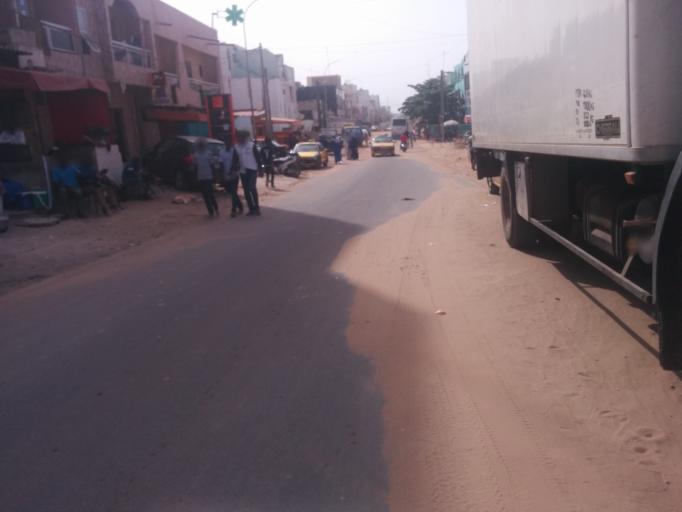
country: SN
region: Dakar
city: Pikine
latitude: 14.7645
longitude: -17.4388
